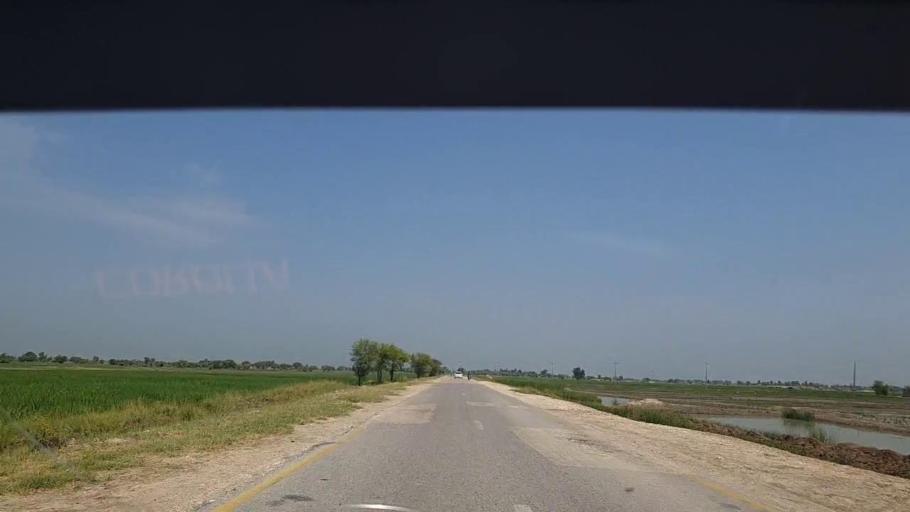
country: PK
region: Sindh
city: Rustam jo Goth
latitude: 28.0988
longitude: 68.8021
